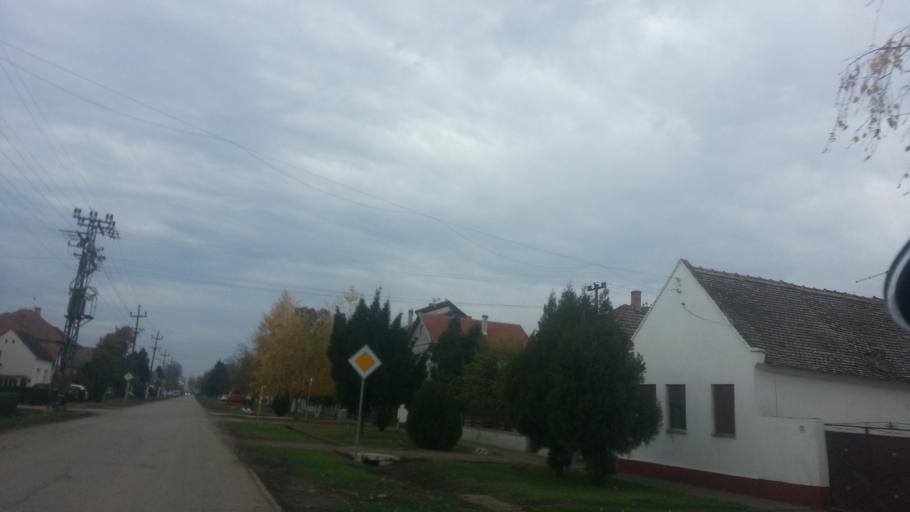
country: RS
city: Golubinci
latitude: 44.9921
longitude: 20.0617
